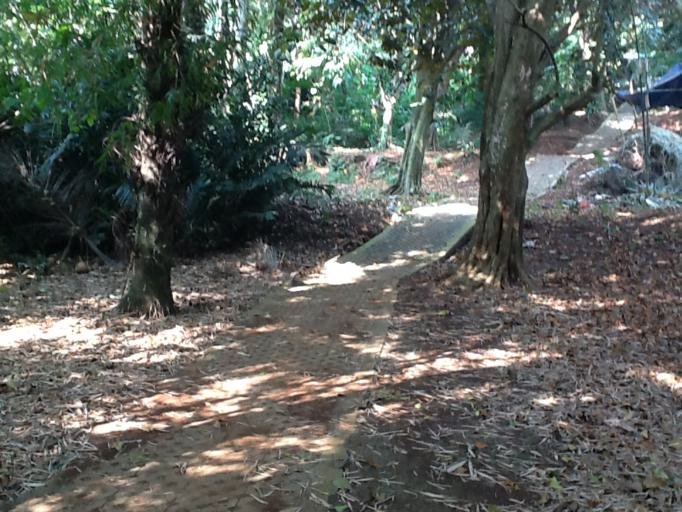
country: ID
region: West Java
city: Pamulang
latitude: -6.3123
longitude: 106.7773
